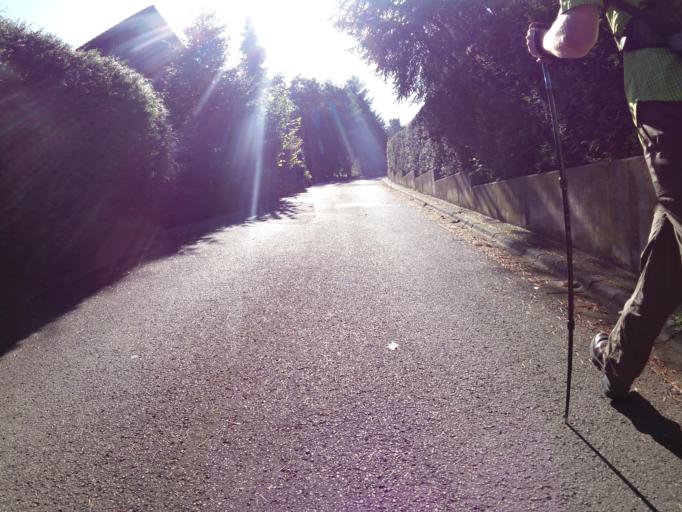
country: DE
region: Rheinland-Pfalz
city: Waldbockelheim
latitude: 49.8150
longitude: 7.7223
